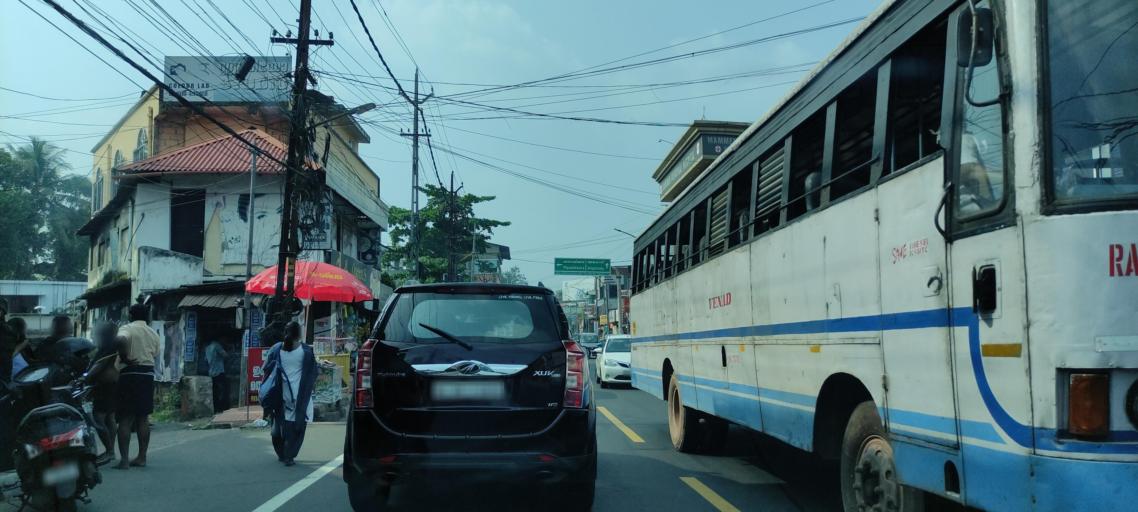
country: IN
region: Kerala
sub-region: Alappuzha
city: Chengannur
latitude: 9.3194
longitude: 76.6118
